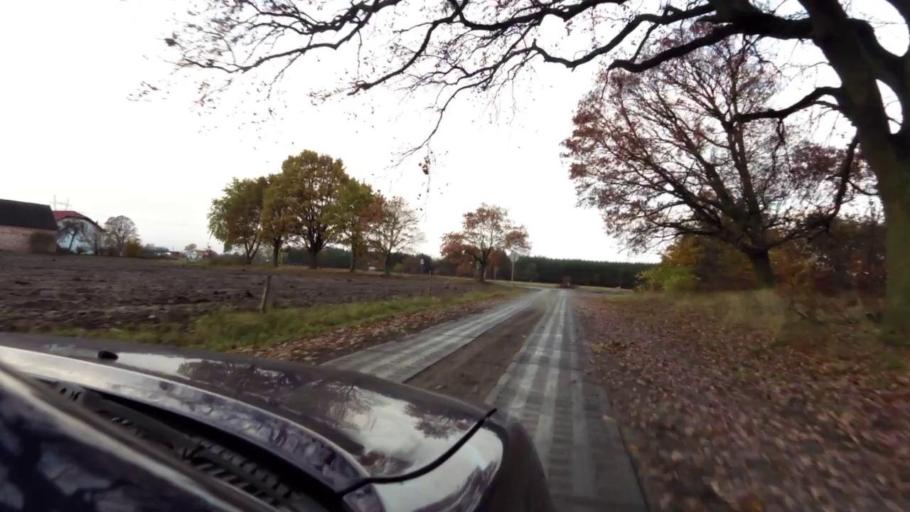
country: PL
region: West Pomeranian Voivodeship
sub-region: Powiat goleniowski
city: Goleniow
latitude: 53.5826
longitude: 14.7652
